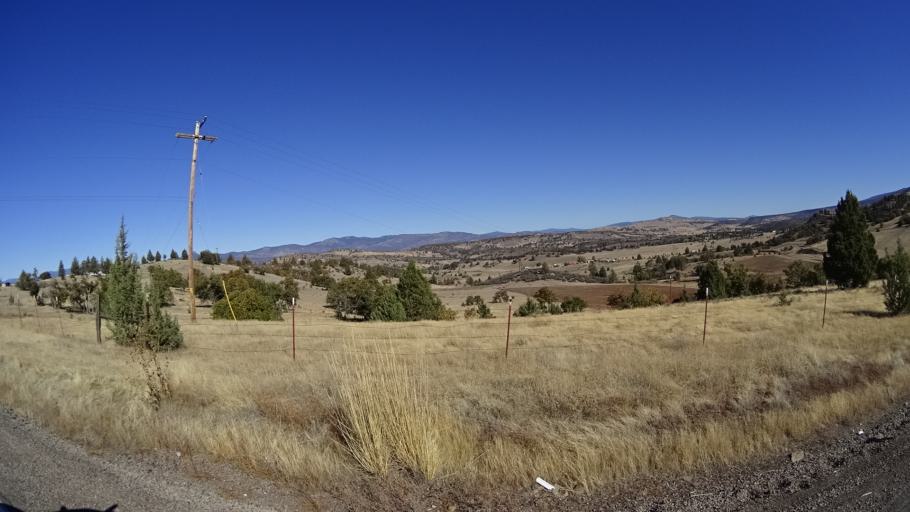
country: US
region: California
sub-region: Siskiyou County
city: Montague
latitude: 41.8705
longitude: -122.4267
